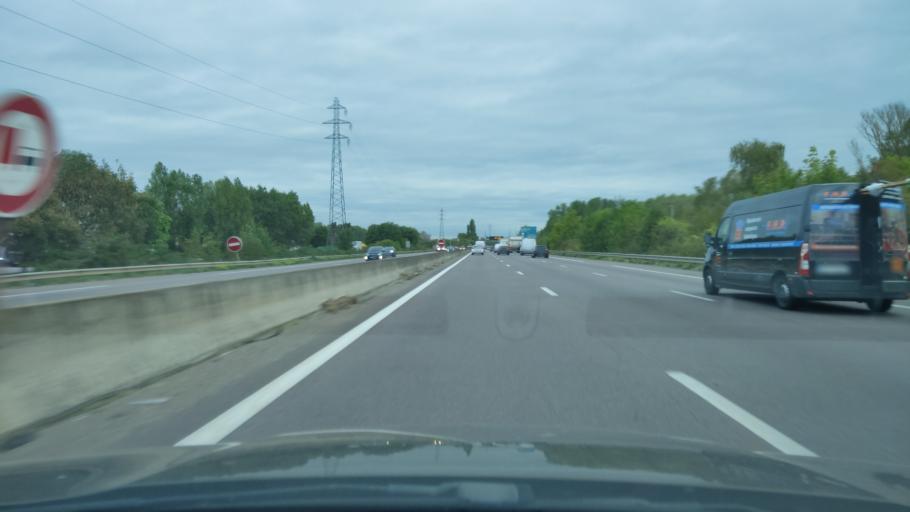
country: FR
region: Lorraine
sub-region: Departement de la Moselle
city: Argancy
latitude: 49.1786
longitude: 6.1779
